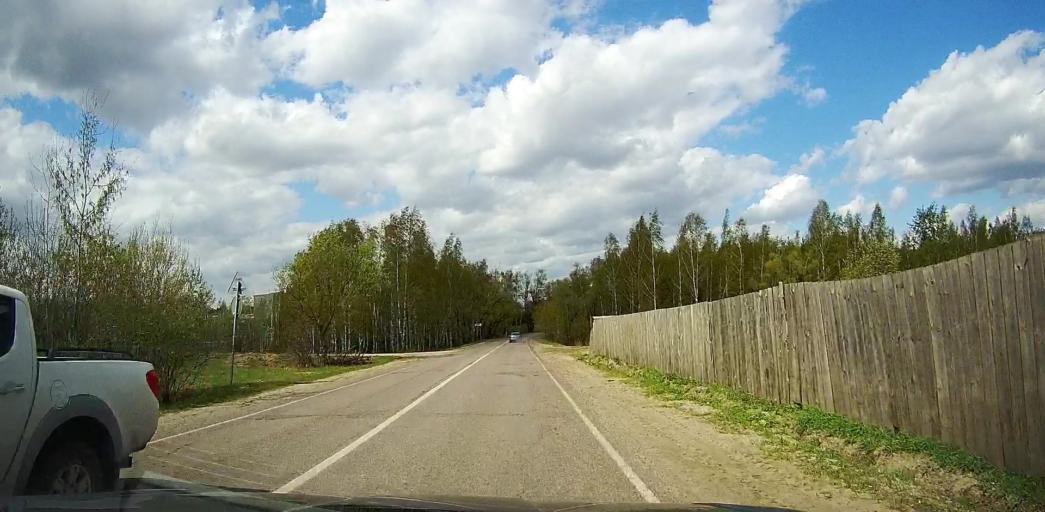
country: RU
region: Moskovskaya
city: Davydovo
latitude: 55.6063
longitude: 38.8479
